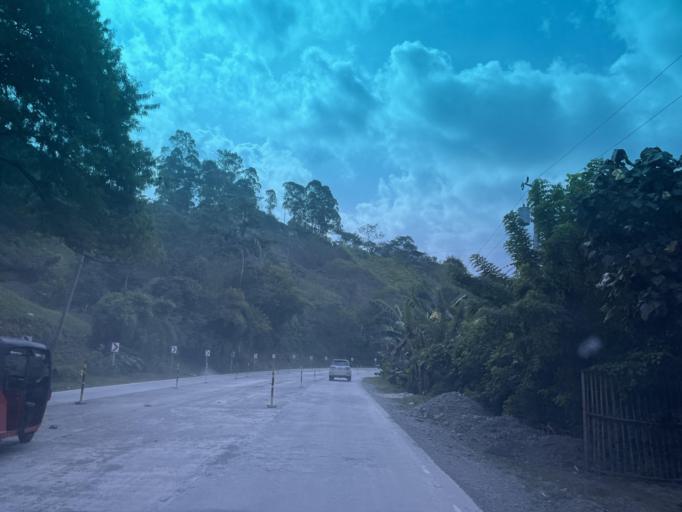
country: PH
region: Davao
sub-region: Province of Davao del Sur
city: Tamugan
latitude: 7.3327
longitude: 125.2942
